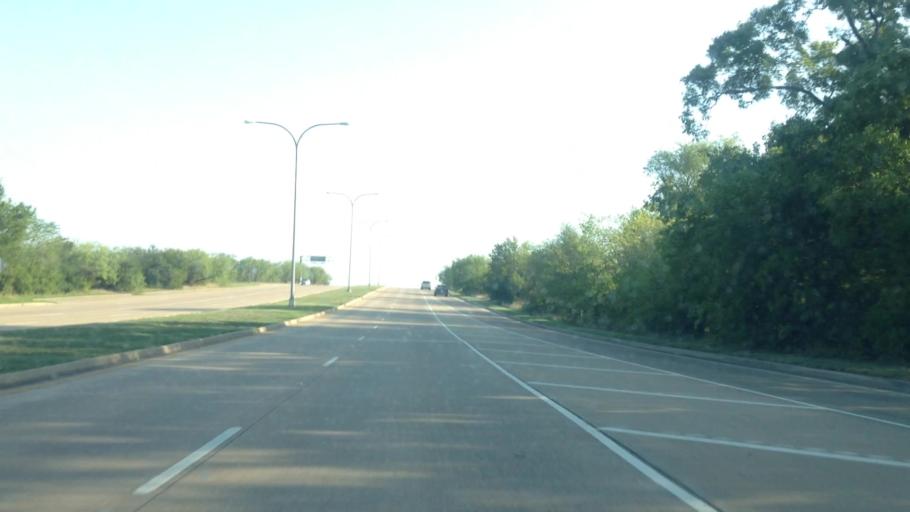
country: US
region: Texas
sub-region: Tarrant County
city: Pantego
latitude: 32.7341
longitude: -97.1813
